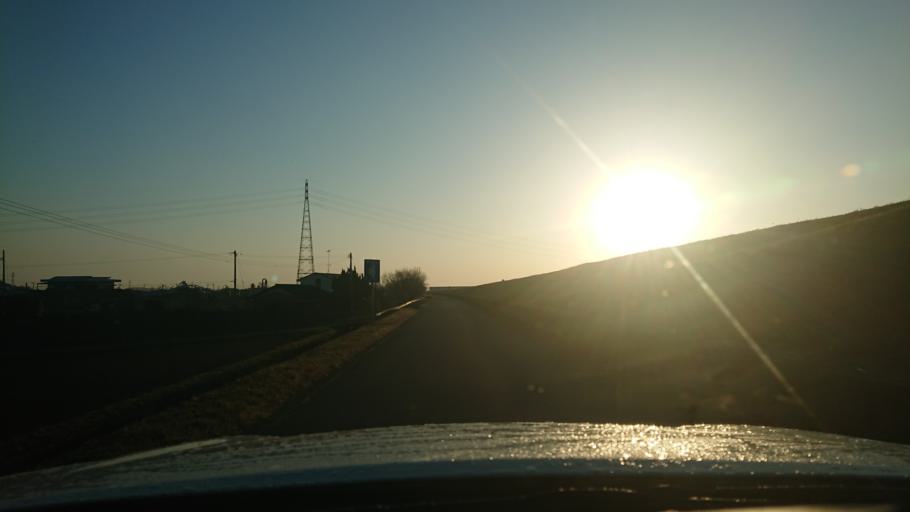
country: JP
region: Tokushima
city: Anan
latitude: 33.9411
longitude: 134.6016
